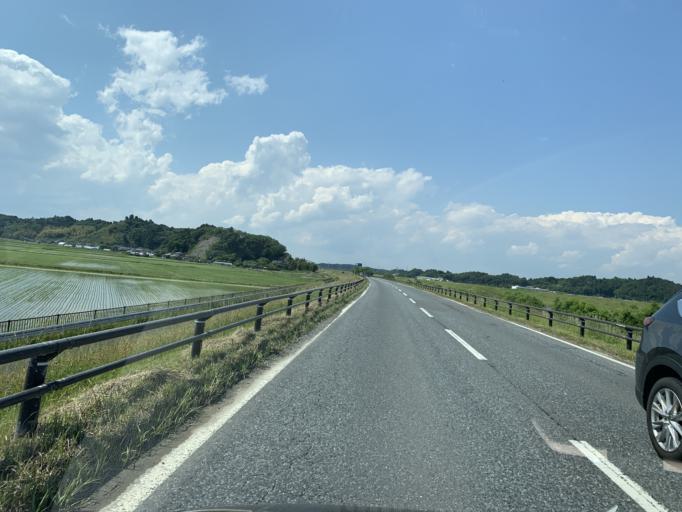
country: JP
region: Miyagi
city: Yamoto
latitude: 38.3978
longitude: 141.1550
